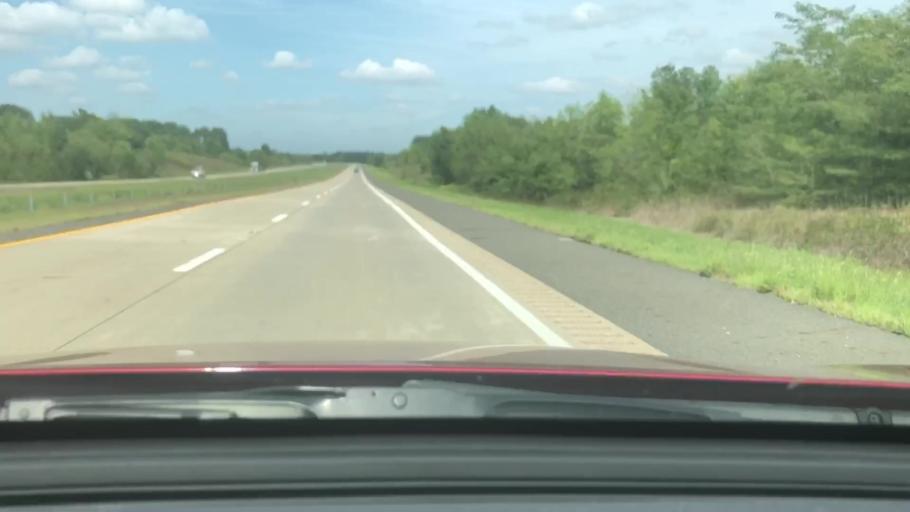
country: US
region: Texas
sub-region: Cass County
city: Queen City
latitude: 33.1589
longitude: -93.8872
